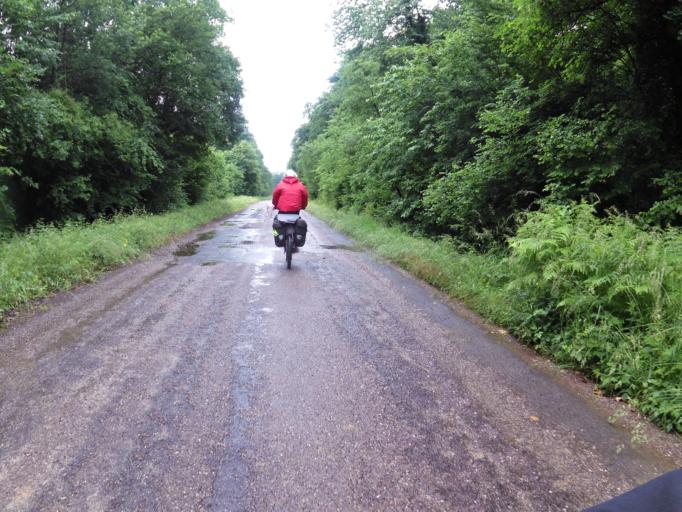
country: FR
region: Champagne-Ardenne
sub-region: Departement de la Marne
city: Sermaize-les-Bains
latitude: 48.7642
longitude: 4.9448
